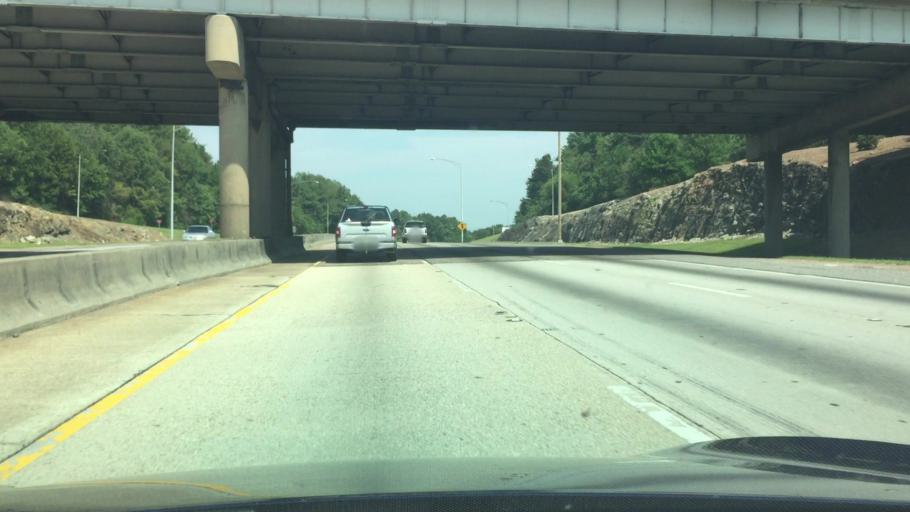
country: US
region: Alabama
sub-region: Jefferson County
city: Hoover
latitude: 33.4315
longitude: -86.8232
